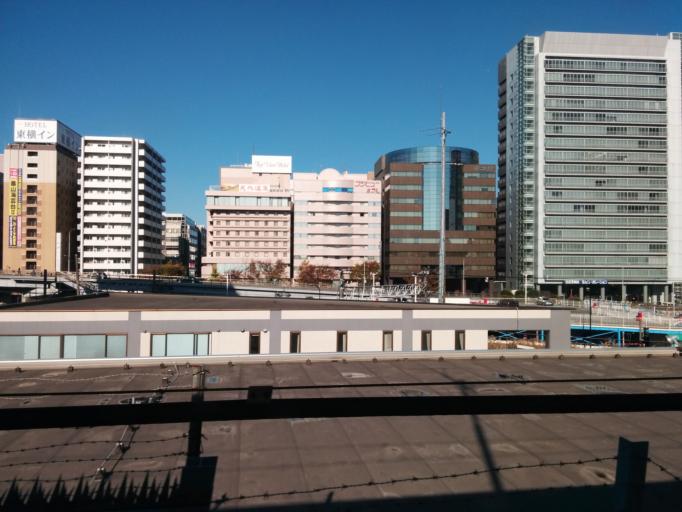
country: JP
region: Kanagawa
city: Yokohama
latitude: 35.5062
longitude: 139.6158
